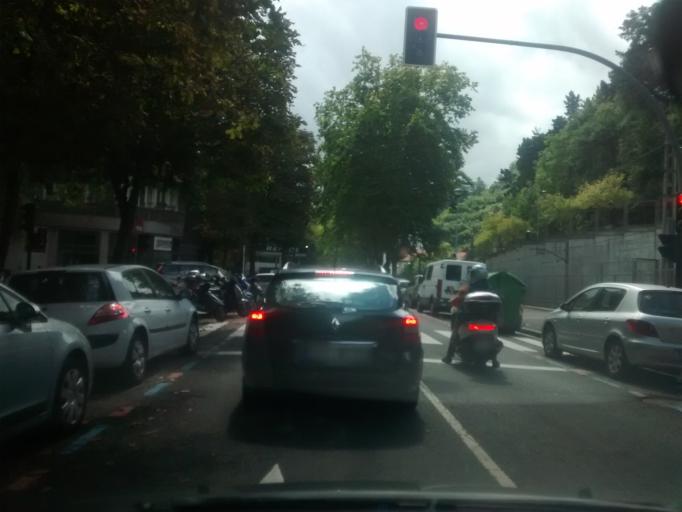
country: ES
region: Basque Country
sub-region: Provincia de Guipuzcoa
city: San Sebastian
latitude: 43.3100
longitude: -1.9816
